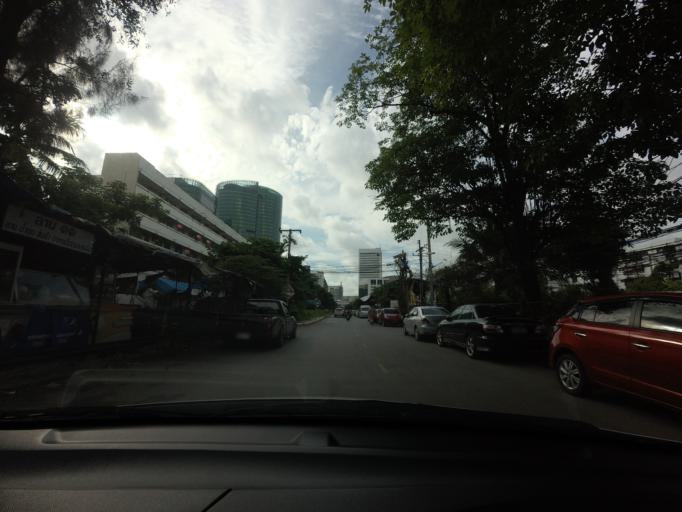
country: TH
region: Bangkok
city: Chatuchak
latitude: 13.8195
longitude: 100.5542
